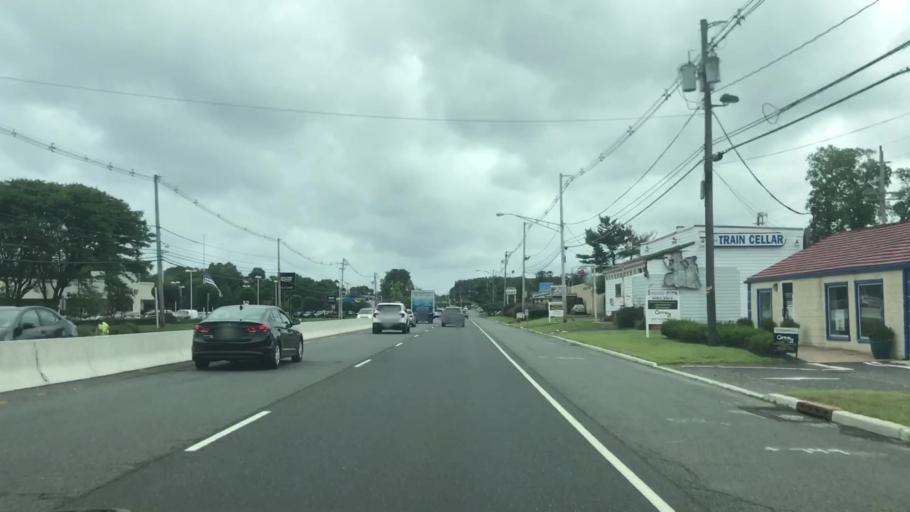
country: US
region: New Jersey
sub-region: Monmouth County
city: Oakhurst
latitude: 40.2696
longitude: -74.0426
